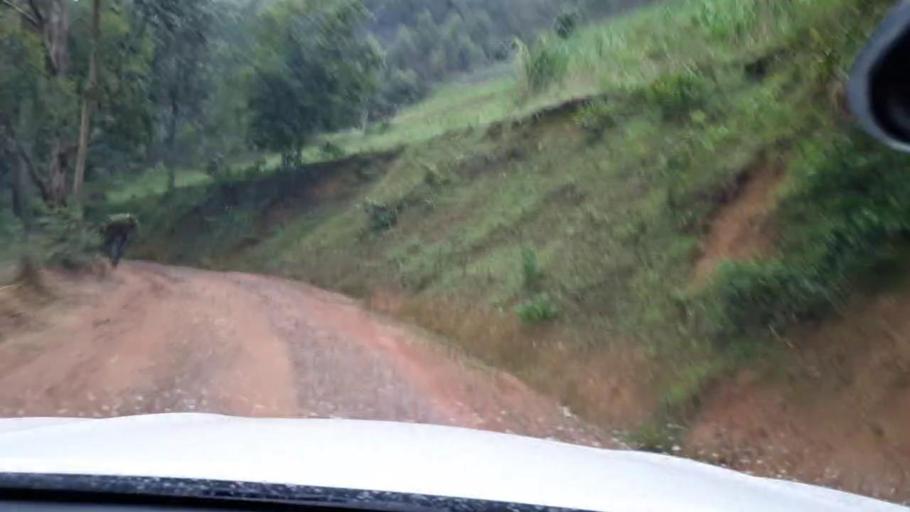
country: RW
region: Western Province
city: Cyangugu
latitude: -2.4089
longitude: 29.2010
